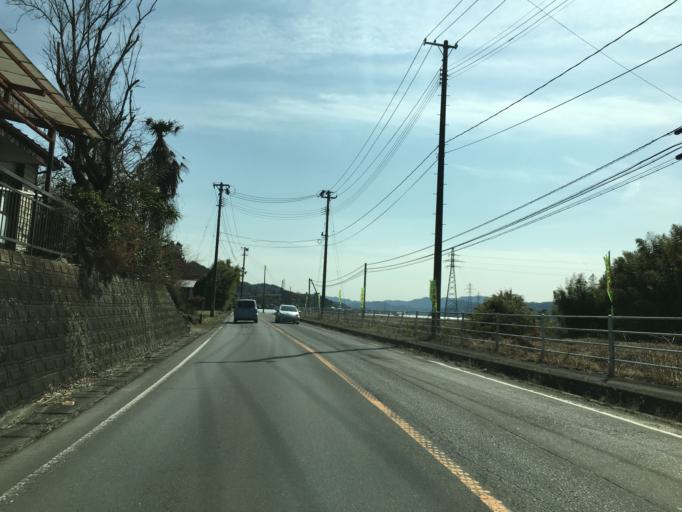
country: JP
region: Ibaraki
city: Daigo
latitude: 36.9249
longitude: 140.4149
